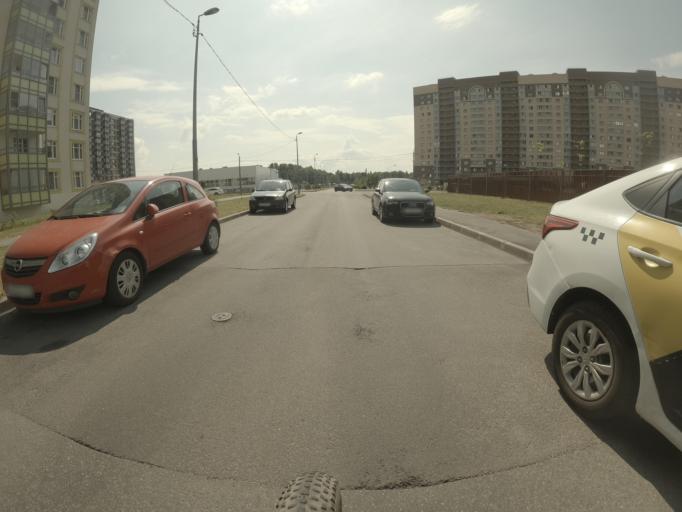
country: RU
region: St.-Petersburg
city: Krasnogvargeisky
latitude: 59.9157
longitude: 30.4376
